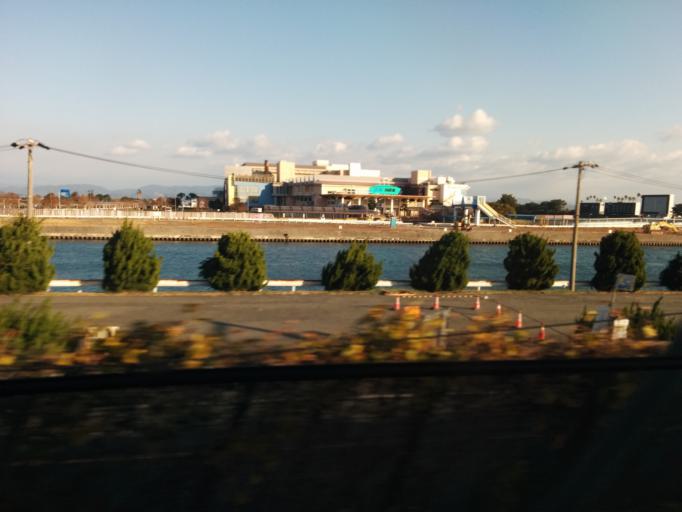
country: JP
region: Shizuoka
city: Kosai-shi
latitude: 34.6947
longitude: 137.5710
